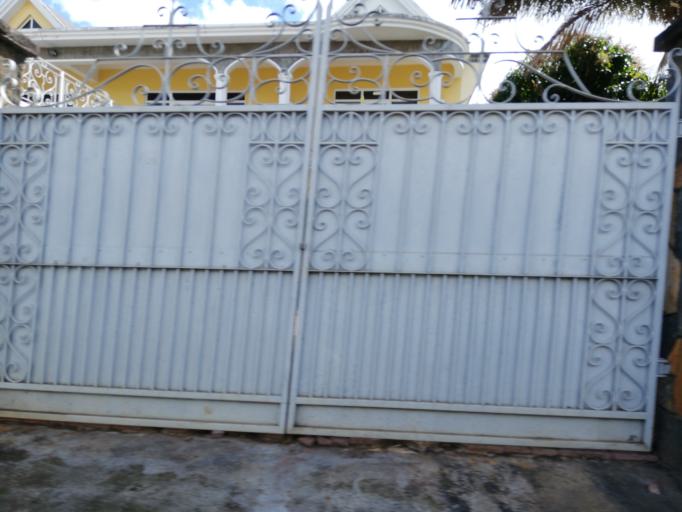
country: MU
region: Moka
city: Pailles
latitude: -20.1961
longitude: 57.4673
